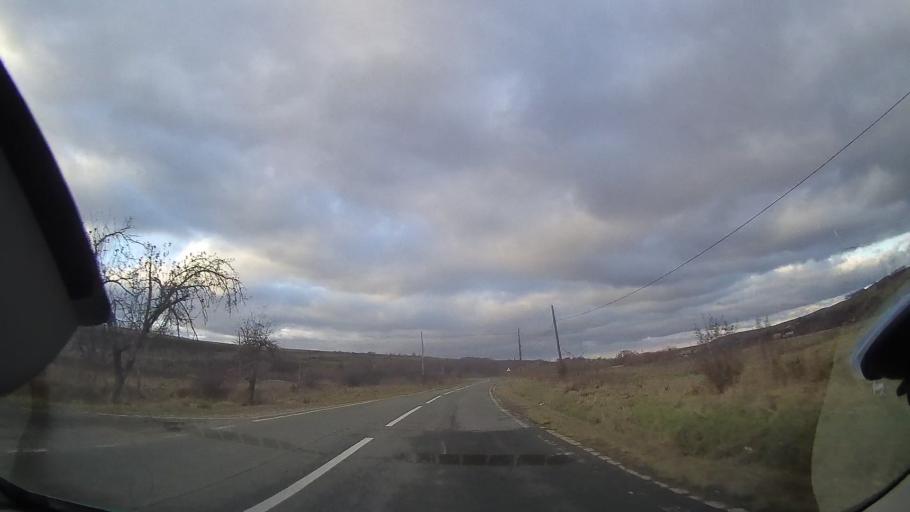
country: RO
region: Cluj
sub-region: Comuna Calatele
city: Calatele
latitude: 46.7930
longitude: 22.9966
